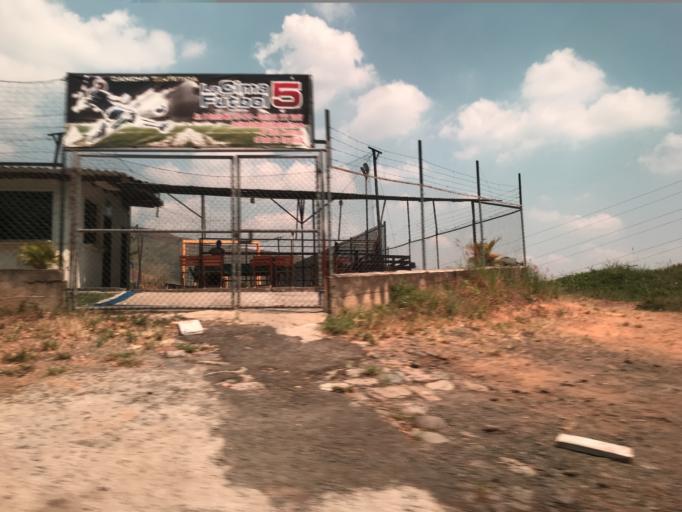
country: CO
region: Valle del Cauca
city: Cali
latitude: 3.4572
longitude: -76.5821
